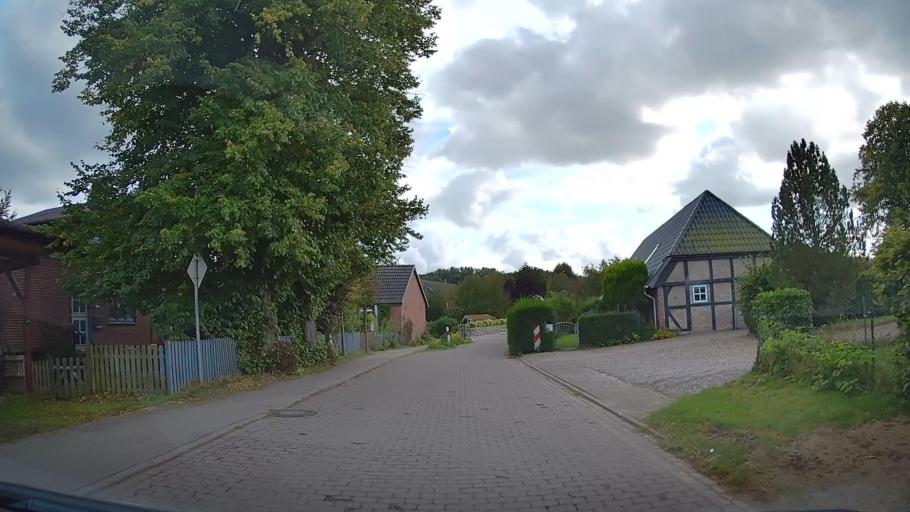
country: DE
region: Schleswig-Holstein
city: Steinberg
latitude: 54.7776
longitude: 9.7999
